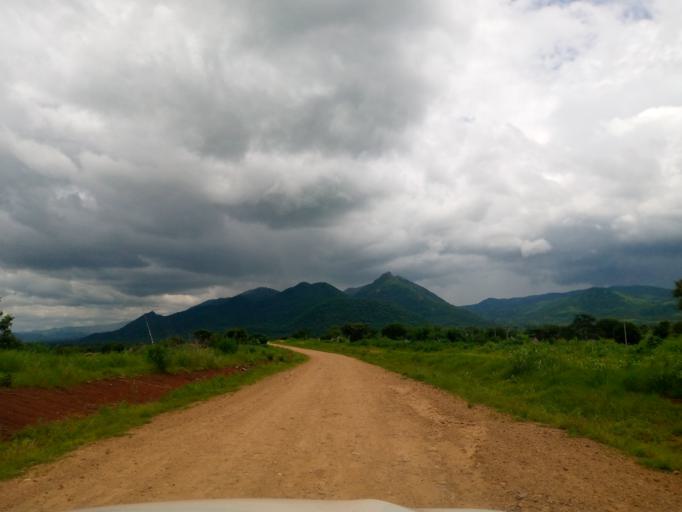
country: ET
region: Oromiya
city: Mendi
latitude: 10.1892
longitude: 35.0933
